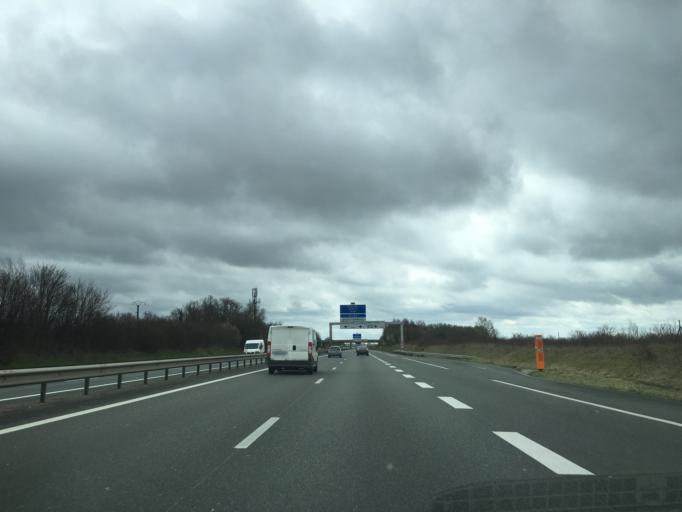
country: FR
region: Ile-de-France
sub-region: Departement de Seine-et-Marne
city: Moissy-Cramayel
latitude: 48.6501
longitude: 2.6199
